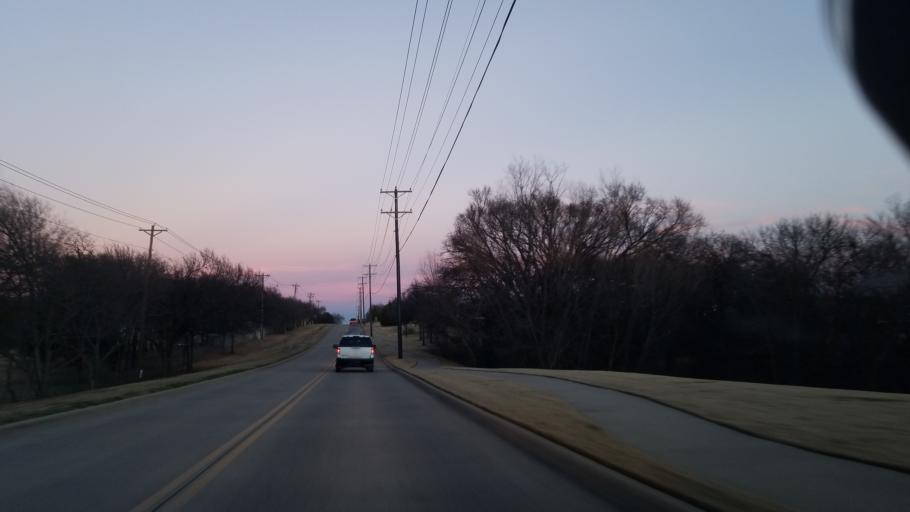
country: US
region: Texas
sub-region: Denton County
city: Corinth
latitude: 33.1584
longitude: -97.1024
